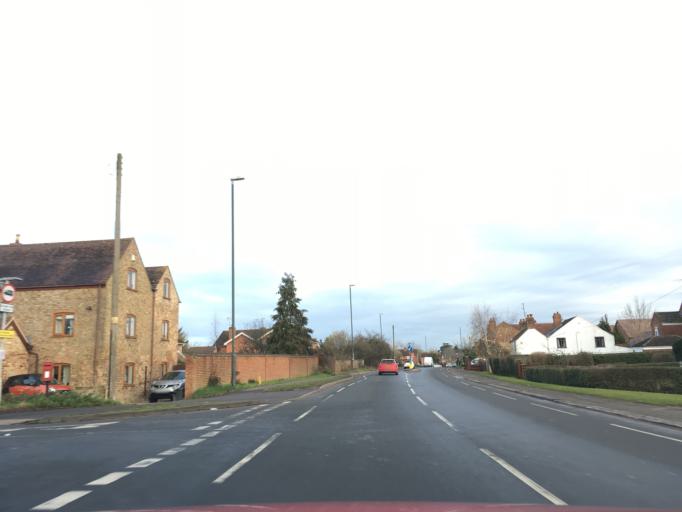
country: GB
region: England
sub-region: Gloucestershire
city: Stonehouse
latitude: 51.8134
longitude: -2.2842
